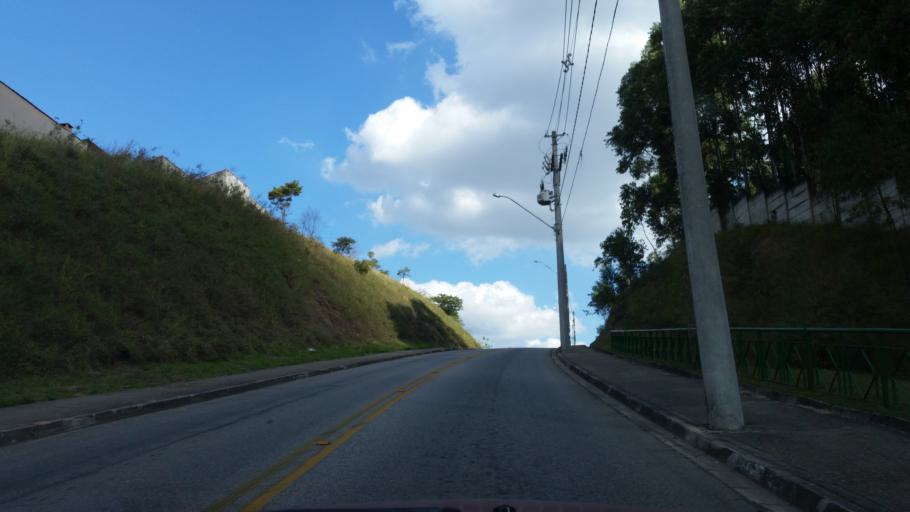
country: BR
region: Sao Paulo
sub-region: Mairinque
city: Mairinque
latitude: -23.5277
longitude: -47.2564
